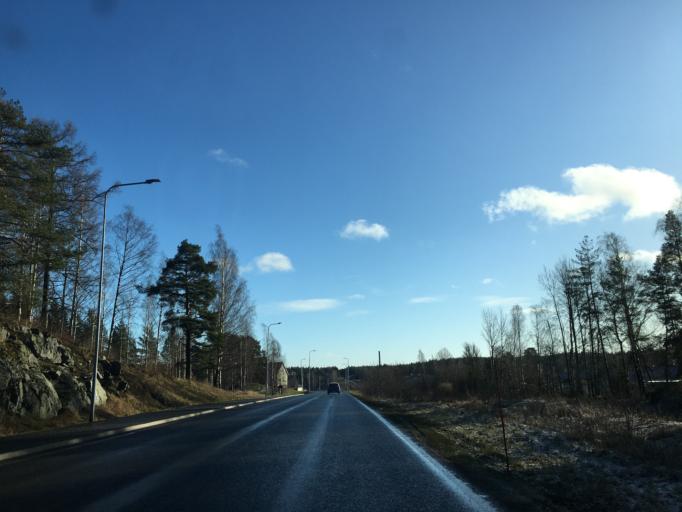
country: FI
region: Varsinais-Suomi
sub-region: Turku
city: Raisio
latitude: 60.4793
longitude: 22.1452
